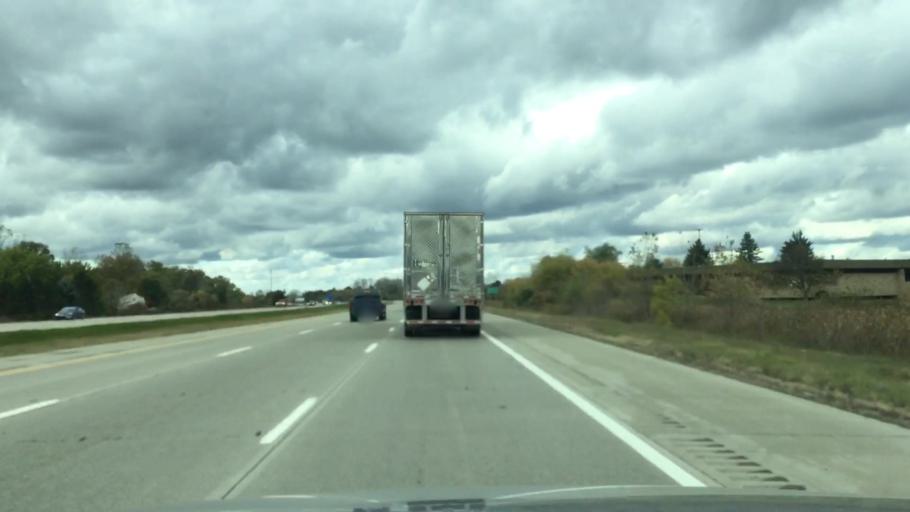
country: US
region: Michigan
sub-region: Genesee County
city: Burton
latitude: 43.0175
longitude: -83.5738
